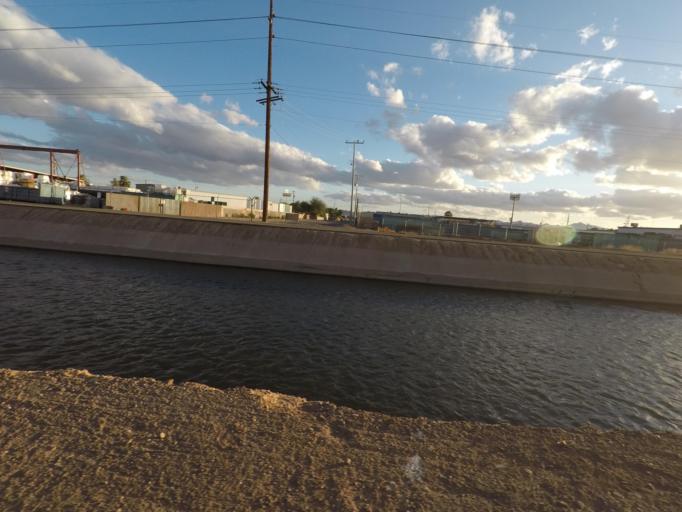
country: US
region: Arizona
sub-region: Maricopa County
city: Phoenix
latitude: 33.4901
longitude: -112.1193
